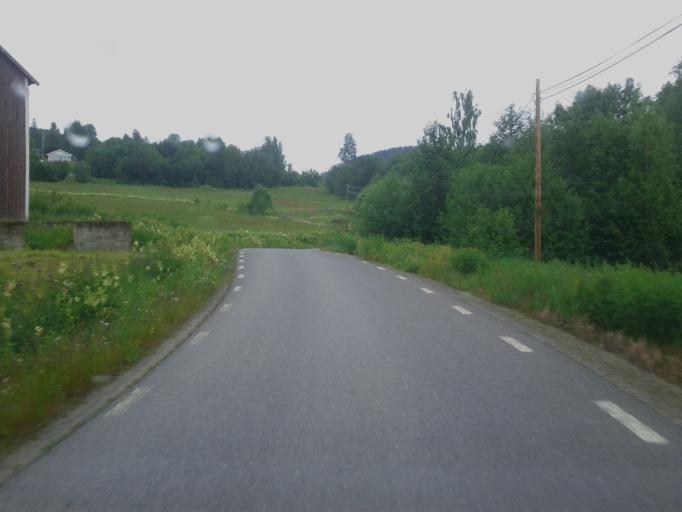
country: SE
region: Vaesternorrland
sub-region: OErnskoeldsviks Kommun
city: Bjasta
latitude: 63.0650
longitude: 18.4165
